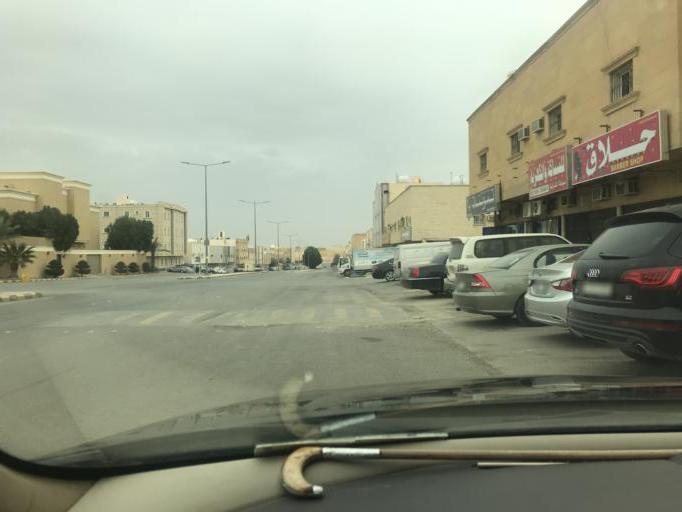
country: SA
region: Ar Riyad
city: Riyadh
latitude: 24.7788
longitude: 46.6977
